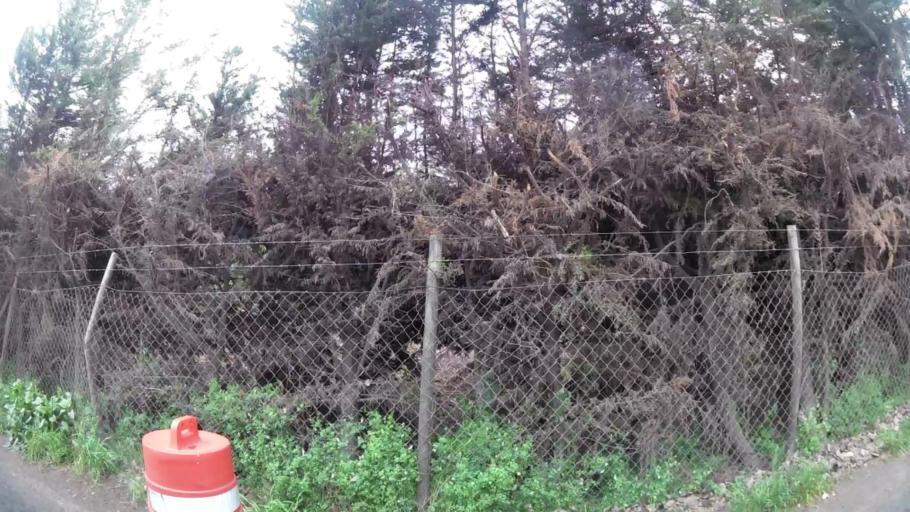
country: CL
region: Santiago Metropolitan
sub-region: Provincia de Chacabuco
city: Lampa
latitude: -33.2428
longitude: -70.7671
